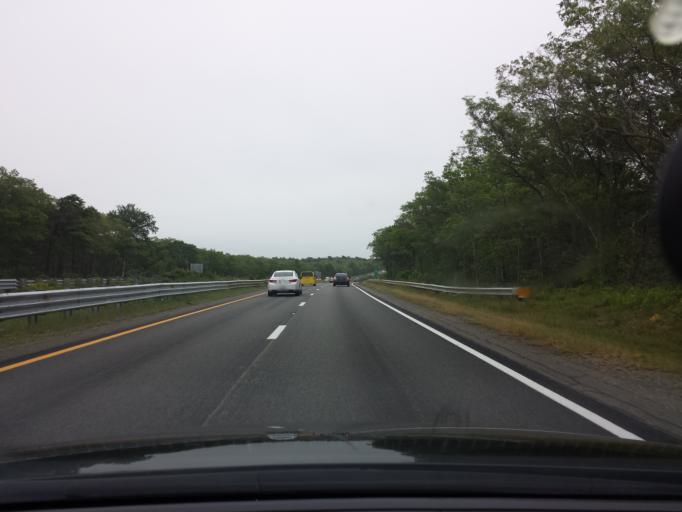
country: US
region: Massachusetts
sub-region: Barnstable County
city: East Sandwich
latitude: 41.7369
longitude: -70.4740
